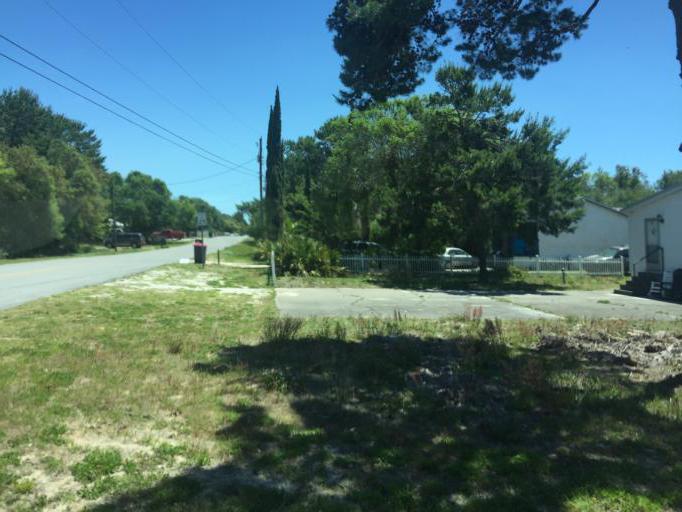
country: US
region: Florida
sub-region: Bay County
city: Laguna Beach
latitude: 30.2655
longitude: -85.9621
